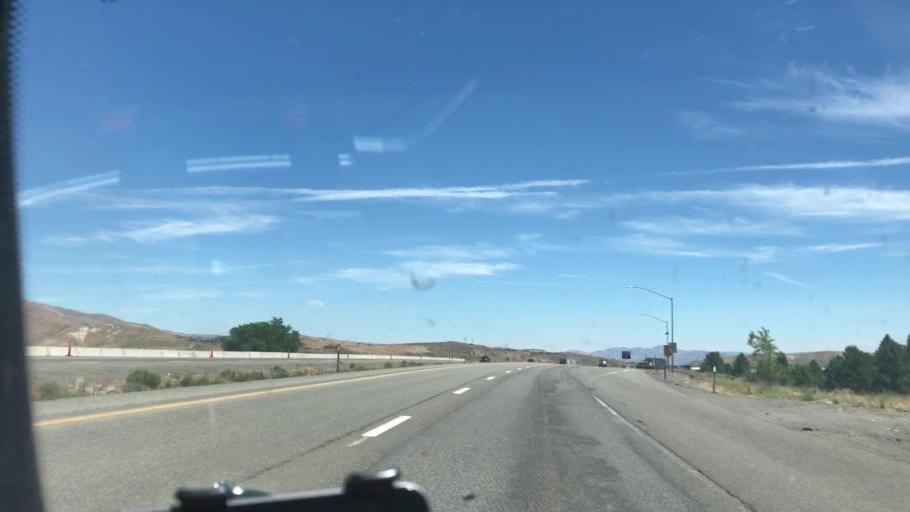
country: US
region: Nevada
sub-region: Washoe County
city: Verdi
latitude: 39.5142
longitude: -119.9840
